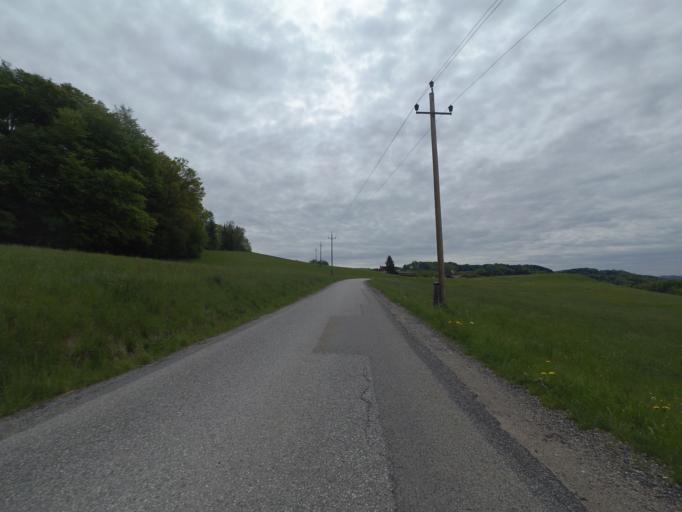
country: AT
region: Salzburg
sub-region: Politischer Bezirk Salzburg-Umgebung
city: Schleedorf
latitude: 47.9917
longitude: 13.1537
